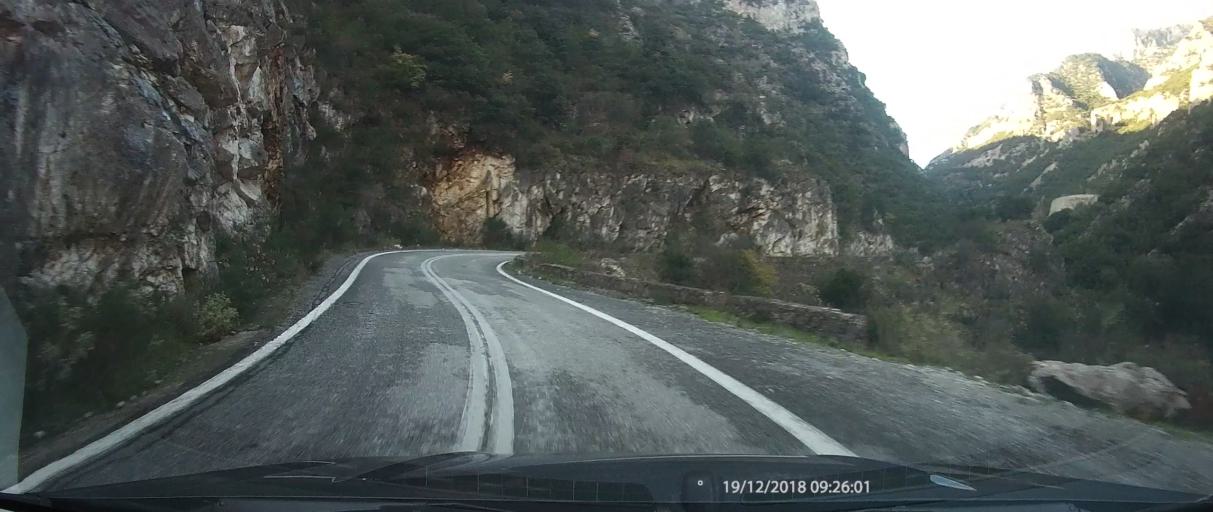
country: GR
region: Peloponnese
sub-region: Nomos Lakonias
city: Magoula
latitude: 37.0934
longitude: 22.3325
